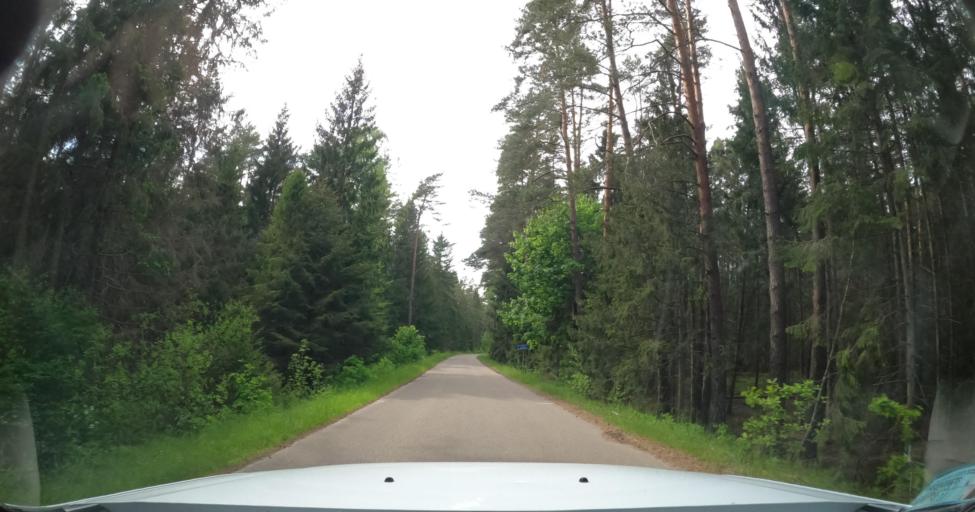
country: PL
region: Warmian-Masurian Voivodeship
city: Dobre Miasto
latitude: 54.1027
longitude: 20.3747
